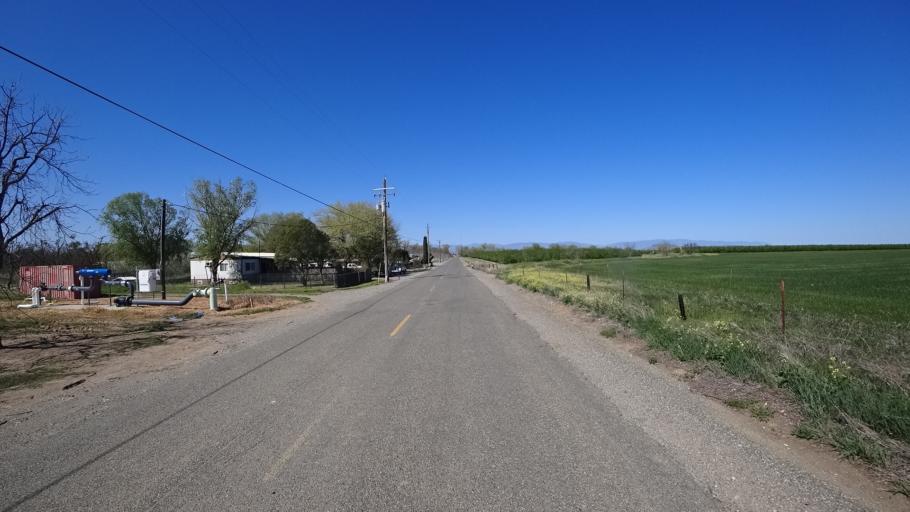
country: US
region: California
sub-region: Glenn County
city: Orland
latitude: 39.6971
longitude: -122.2179
